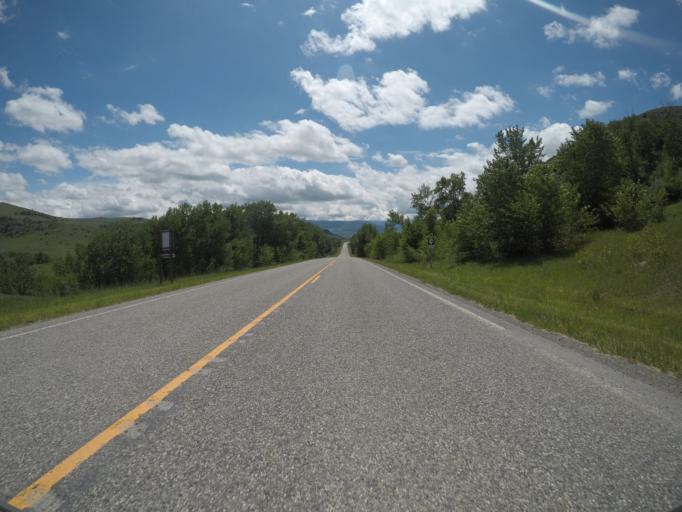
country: US
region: Montana
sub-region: Sweet Grass County
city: Big Timber
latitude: 45.6550
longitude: -110.1141
